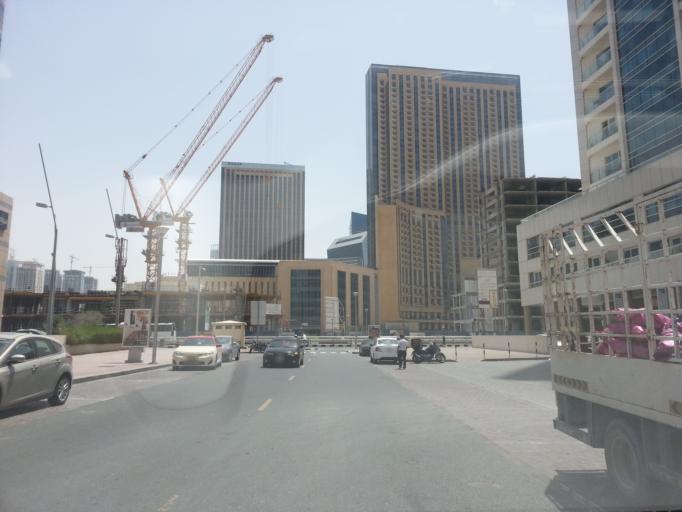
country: AE
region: Dubai
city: Dubai
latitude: 25.0790
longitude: 55.1432
